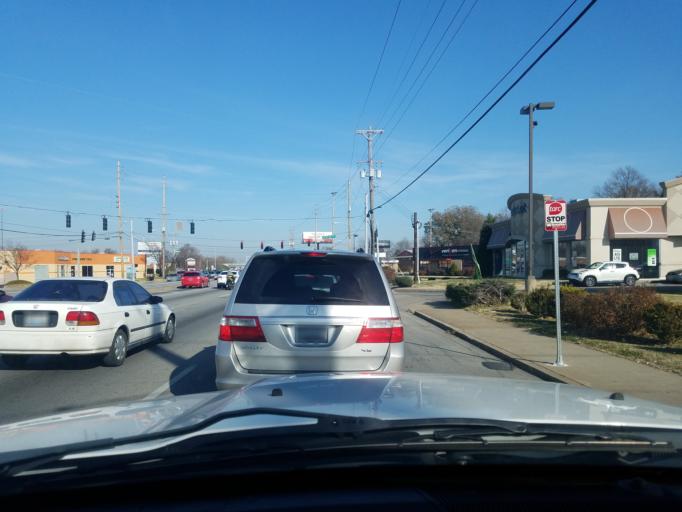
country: US
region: Kentucky
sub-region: Jefferson County
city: Shively
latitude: 38.1803
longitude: -85.8165
